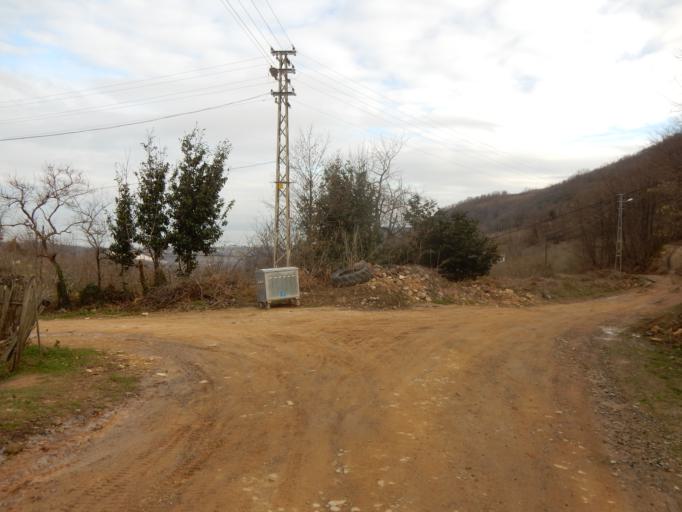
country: TR
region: Ordu
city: Fatsa
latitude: 41.0406
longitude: 37.4219
